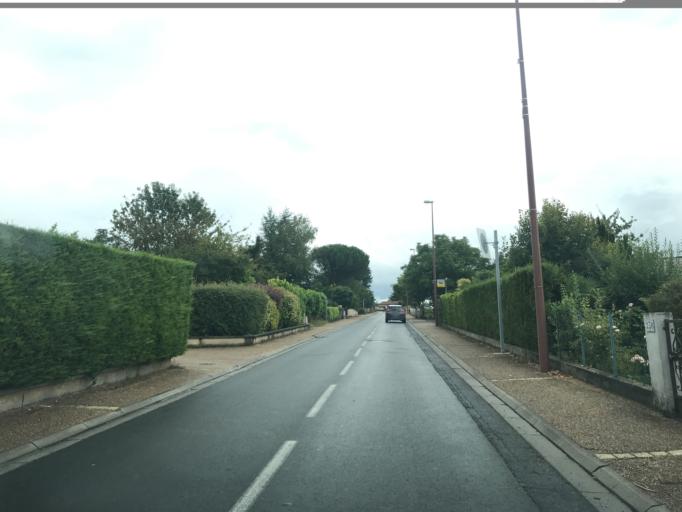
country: FR
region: Aquitaine
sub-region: Departement de la Dordogne
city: Coulounieix-Chamiers
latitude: 45.1594
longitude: 0.6874
